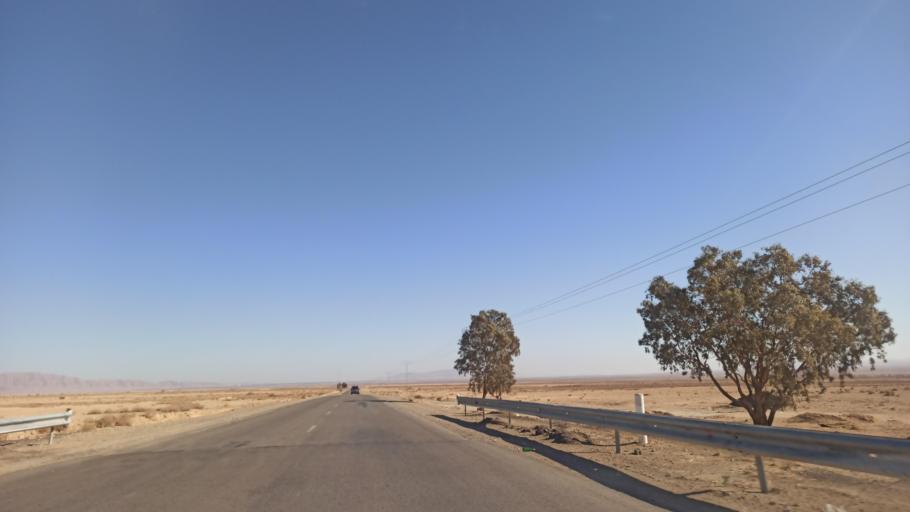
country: TN
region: Gafsa
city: Al Metlaoui
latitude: 34.3194
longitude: 8.5143
